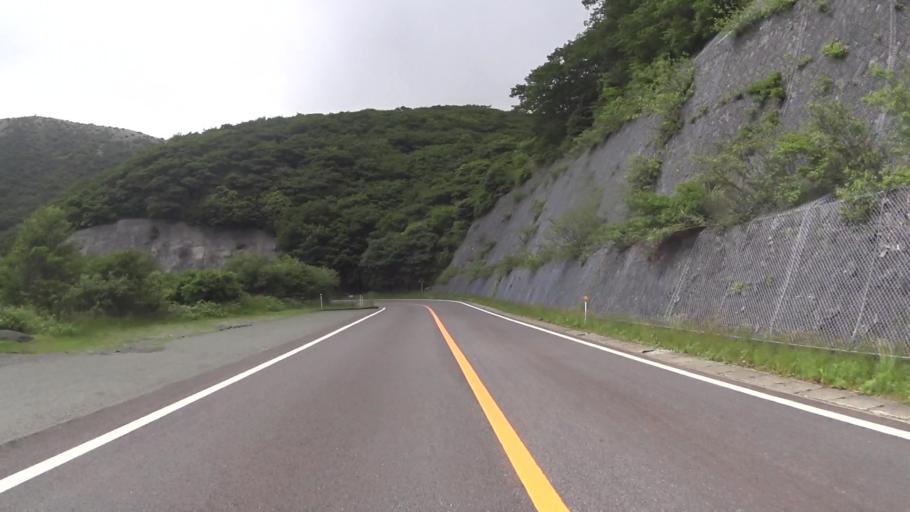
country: JP
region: Kumamoto
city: Aso
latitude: 33.0891
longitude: 131.1949
